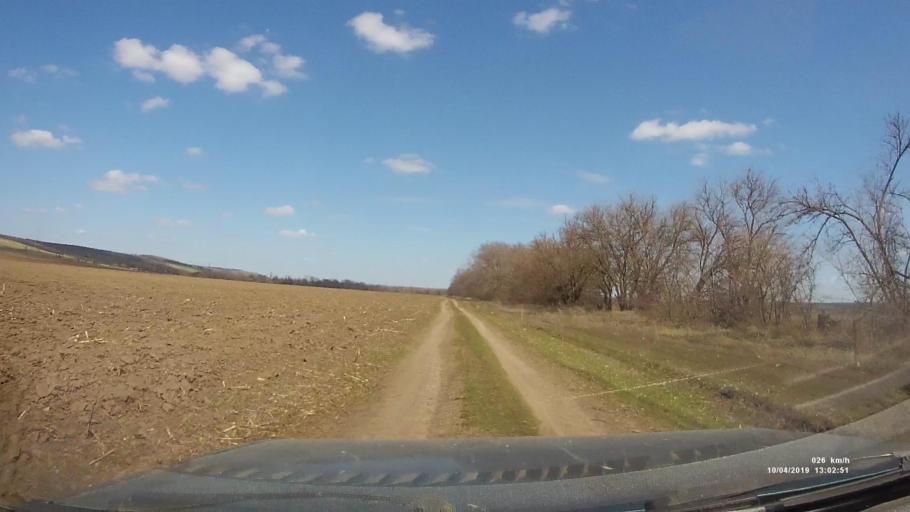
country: RU
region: Rostov
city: Masalovka
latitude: 48.3822
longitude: 40.2318
